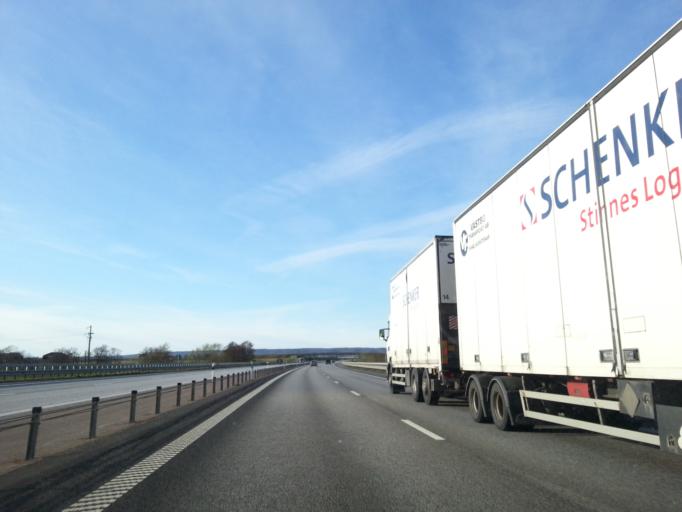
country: SE
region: Skane
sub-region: Angelholms Kommun
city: AEngelholm
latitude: 56.2664
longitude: 12.8940
